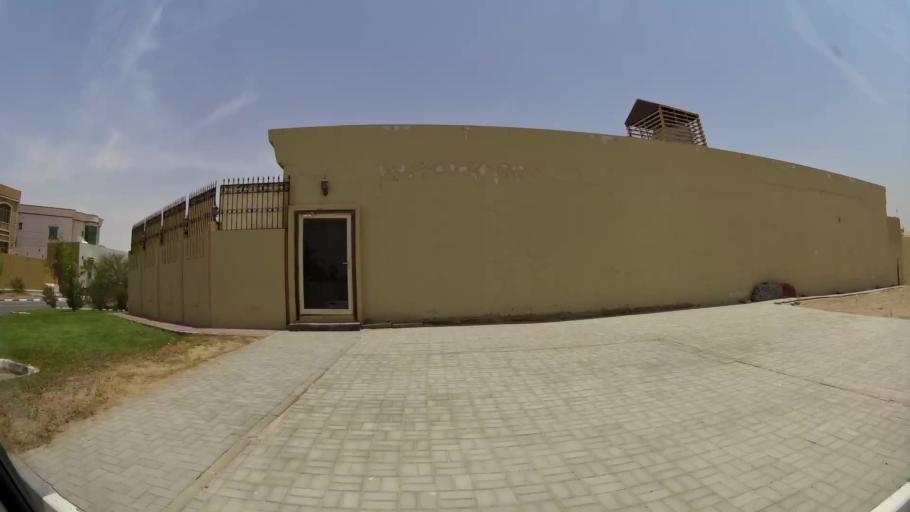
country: AE
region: Ash Shariqah
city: Sharjah
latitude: 25.2543
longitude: 55.4679
